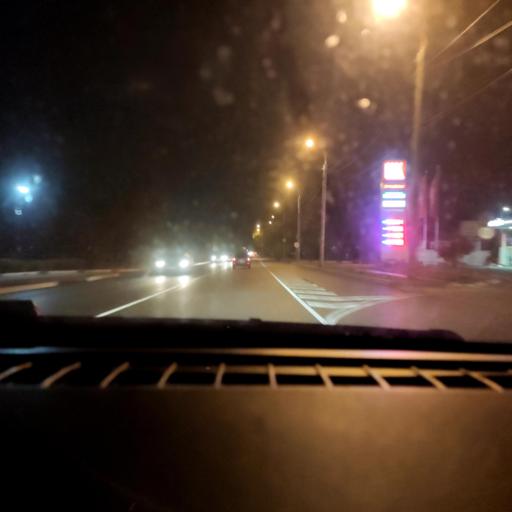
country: RU
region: Voronezj
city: Voronezh
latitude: 51.6569
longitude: 39.2486
